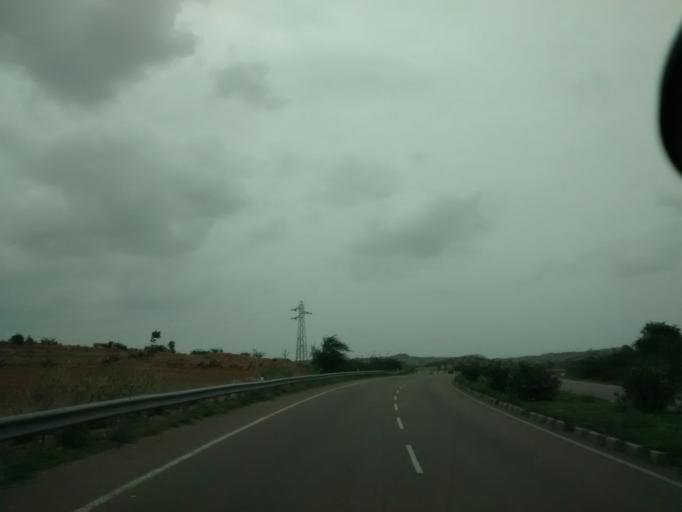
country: IN
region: Andhra Pradesh
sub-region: Kurnool
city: Ramapuram
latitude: 15.1852
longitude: 77.6889
